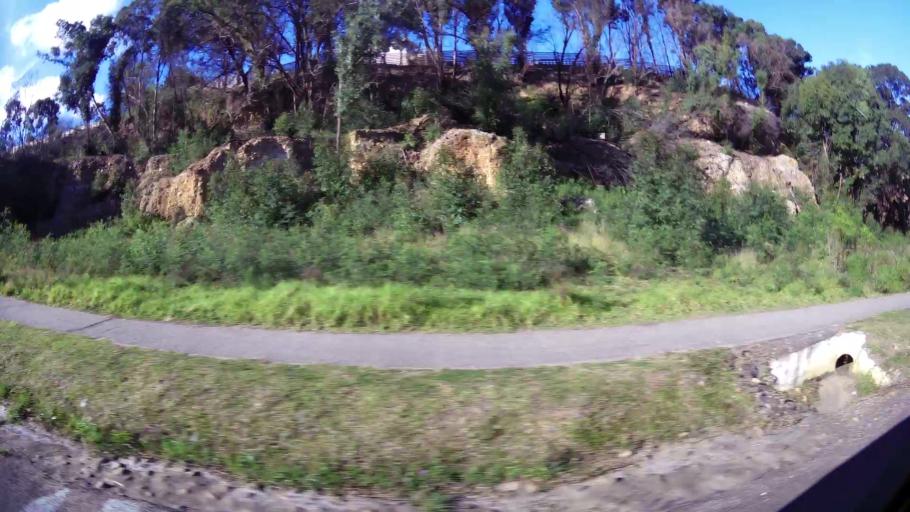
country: ZA
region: Western Cape
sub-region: Eden District Municipality
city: Knysna
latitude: -34.0306
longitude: 23.0482
